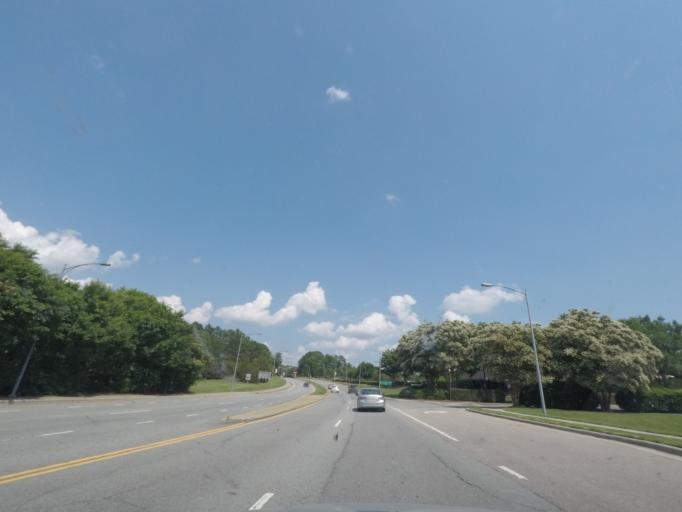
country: US
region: North Carolina
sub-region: Durham County
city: Durham
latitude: 35.9613
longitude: -78.9607
